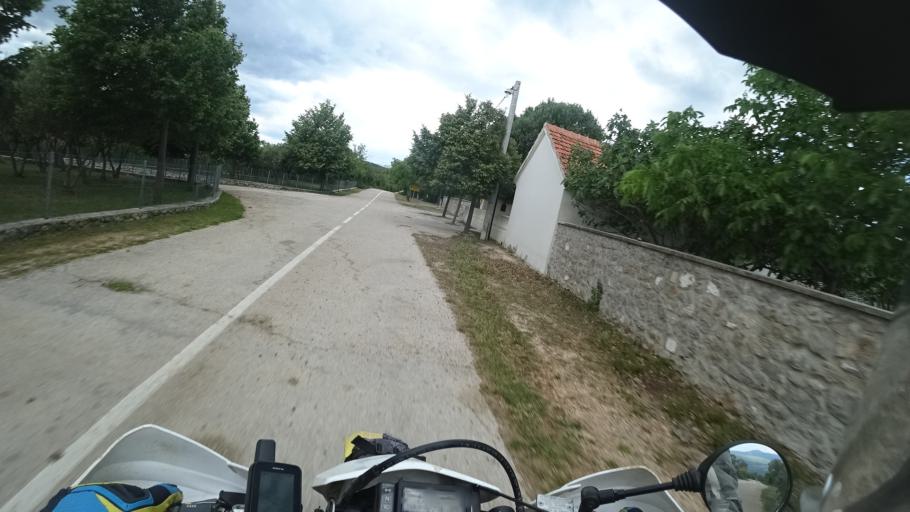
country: HR
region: Zadarska
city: Gracac
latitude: 44.1989
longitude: 15.8705
